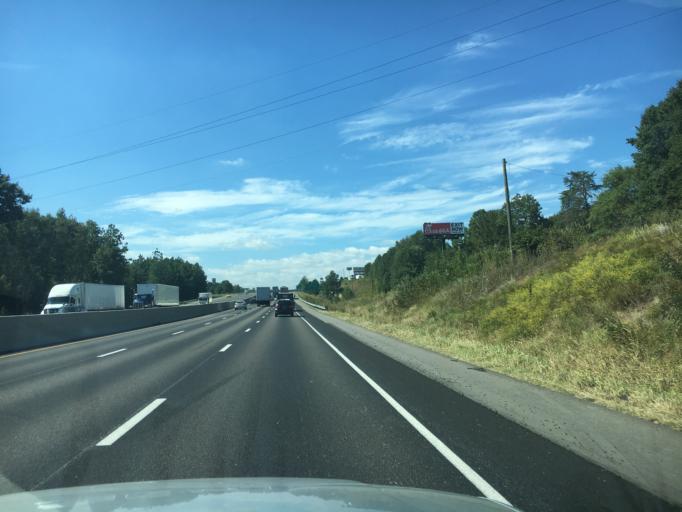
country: US
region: South Carolina
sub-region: Spartanburg County
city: Wellford
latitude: 34.9209
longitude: -82.0969
